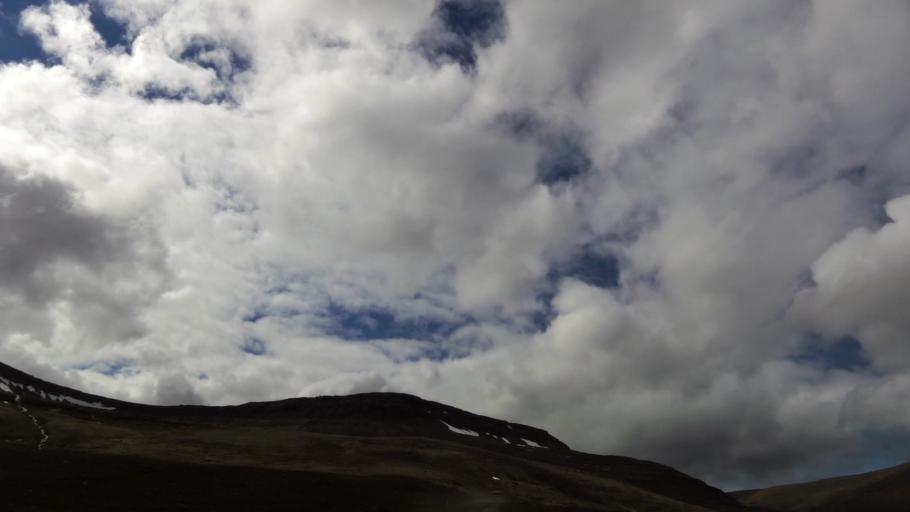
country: IS
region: Westfjords
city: Isafjoerdur
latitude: 66.1643
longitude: -23.3290
